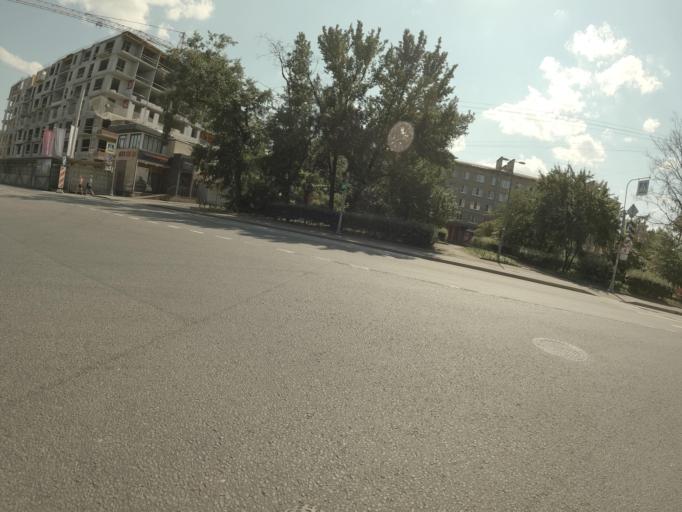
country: RU
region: St.-Petersburg
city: Vasyl'evsky Ostrov
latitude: 59.9092
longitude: 30.2517
